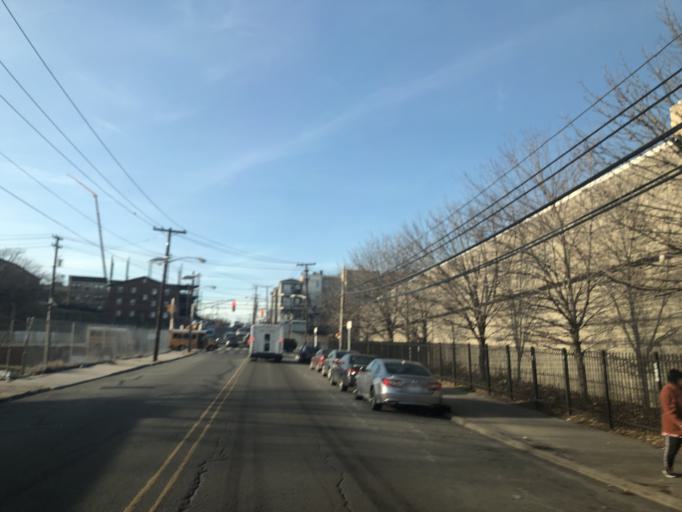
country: US
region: New Jersey
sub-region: Hudson County
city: Jersey City
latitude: 40.7189
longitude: -74.0641
